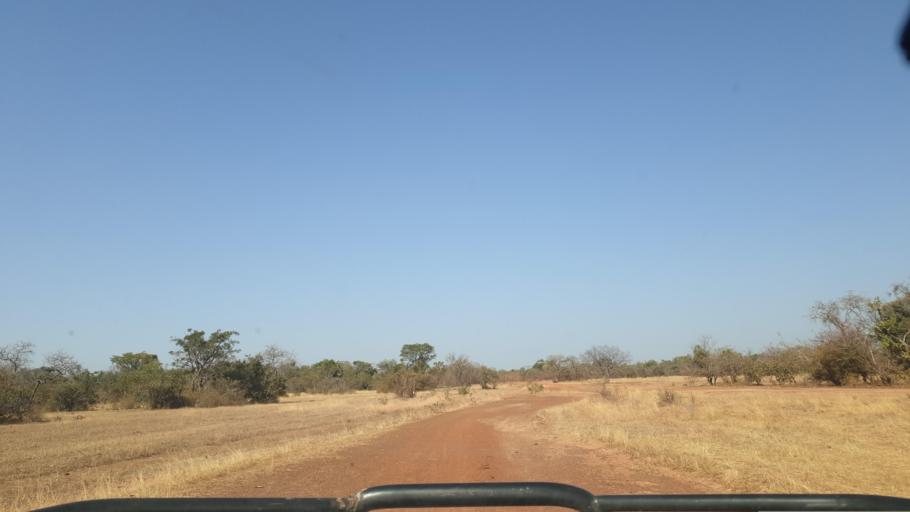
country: ML
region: Sikasso
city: Bougouni
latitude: 11.8195
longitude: -6.9485
